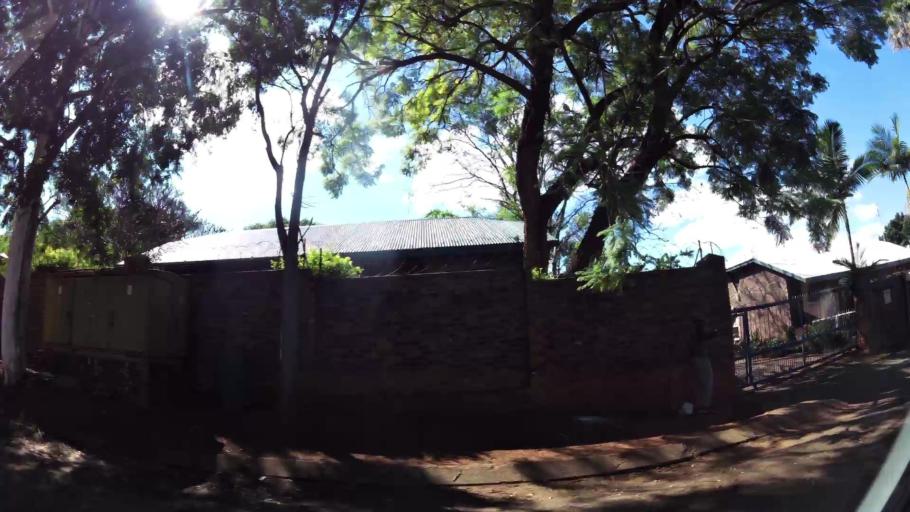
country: ZA
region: Limpopo
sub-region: Mopani District Municipality
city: Tzaneen
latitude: -23.8142
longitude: 30.1523
